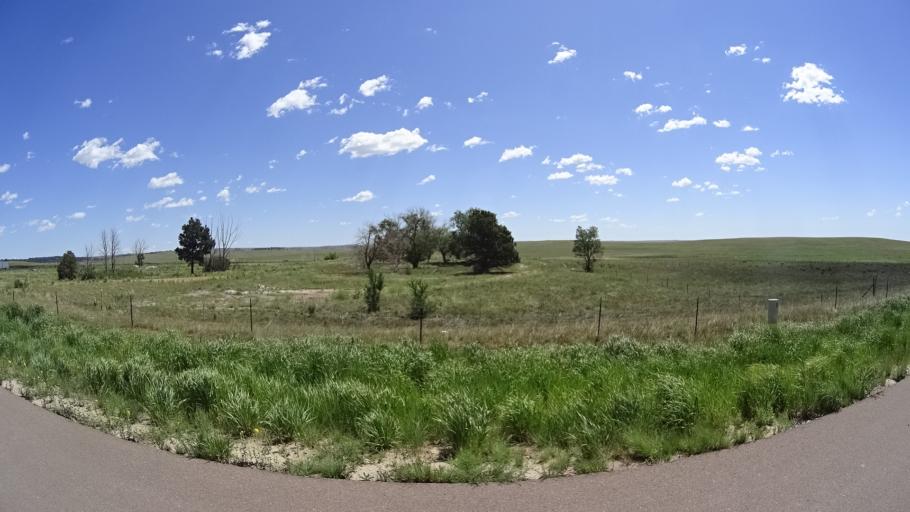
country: US
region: Colorado
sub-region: El Paso County
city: Cimarron Hills
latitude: 38.8313
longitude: -104.6827
